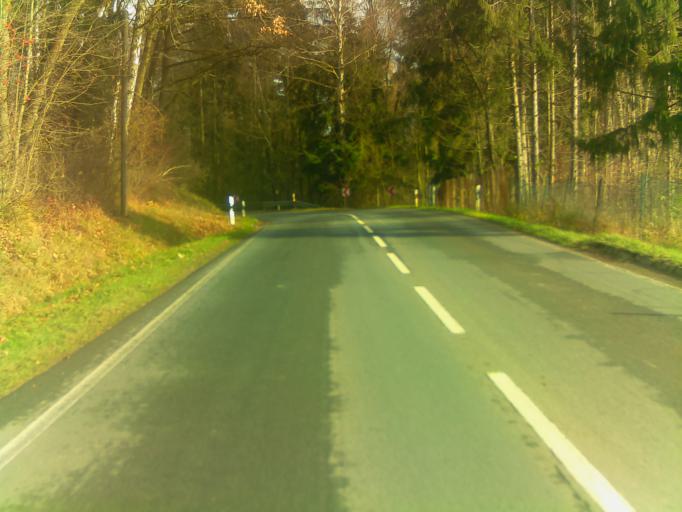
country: DE
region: Thuringia
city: Reurieth
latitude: 50.4067
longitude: 10.6739
